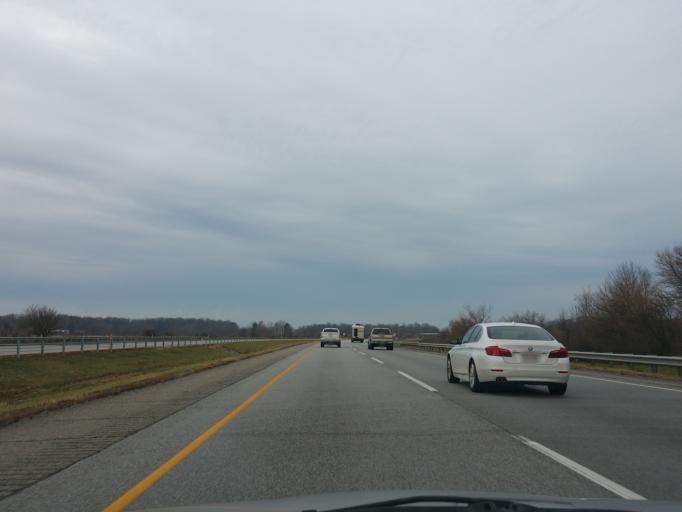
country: US
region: Indiana
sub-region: Porter County
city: Chesterton
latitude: 41.5747
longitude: -87.0556
